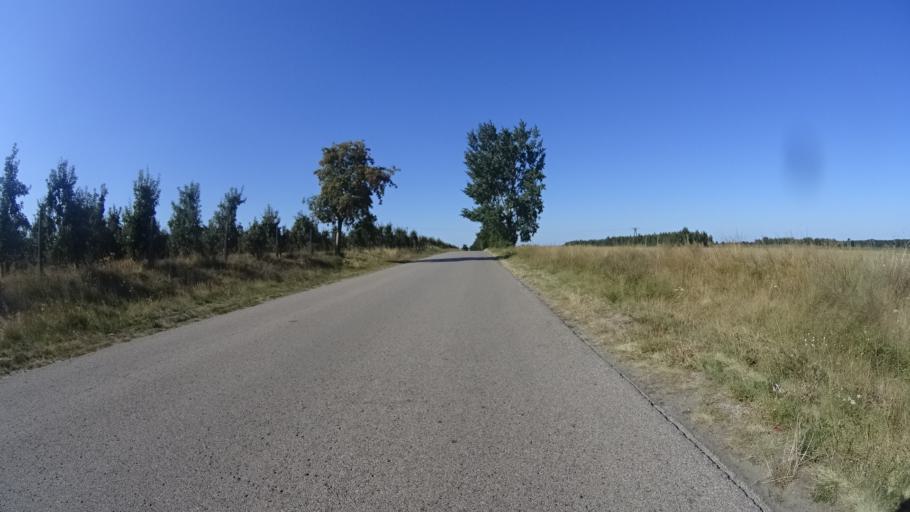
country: PL
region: Masovian Voivodeship
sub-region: Powiat bialobrzeski
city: Wysmierzyce
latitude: 51.6635
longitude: 20.8311
